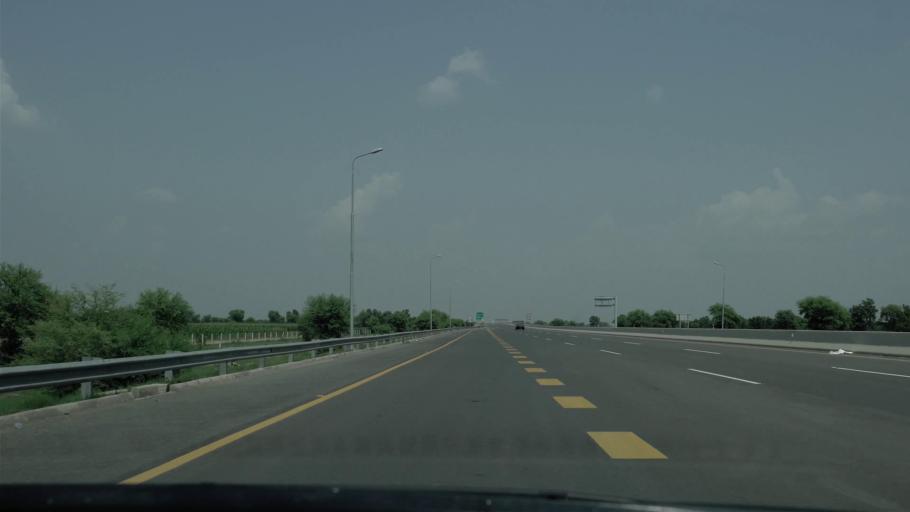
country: PK
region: Punjab
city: Gojra
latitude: 31.1862
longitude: 72.6440
